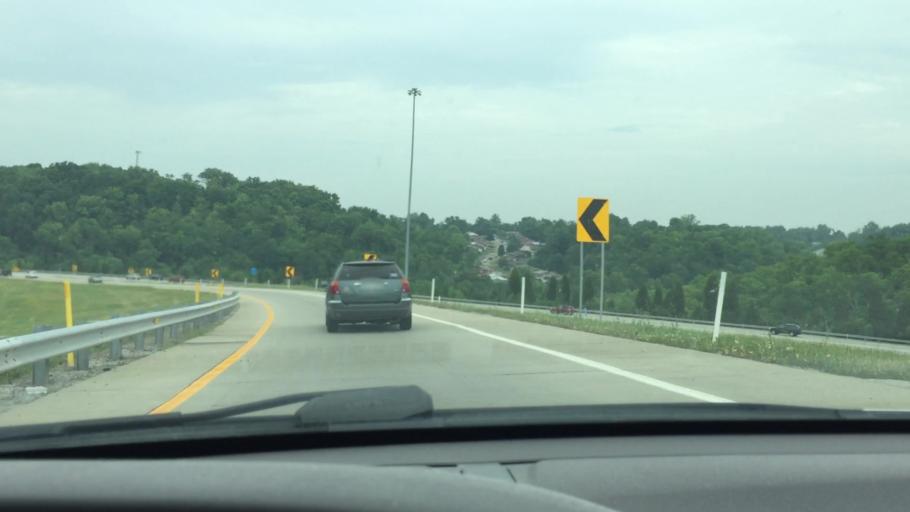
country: US
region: Kentucky
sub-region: Campbell County
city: Highland Heights
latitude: 39.0483
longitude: -84.4627
